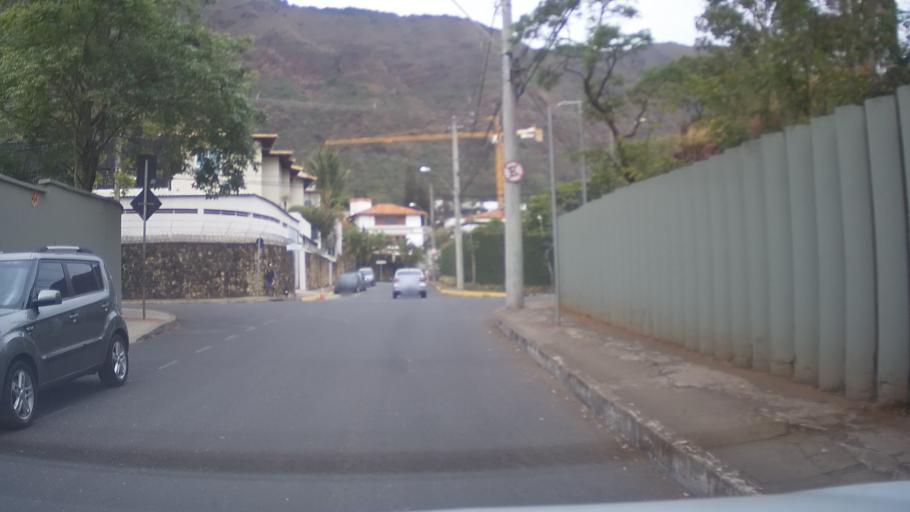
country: BR
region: Minas Gerais
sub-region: Belo Horizonte
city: Belo Horizonte
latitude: -19.9560
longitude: -43.9118
